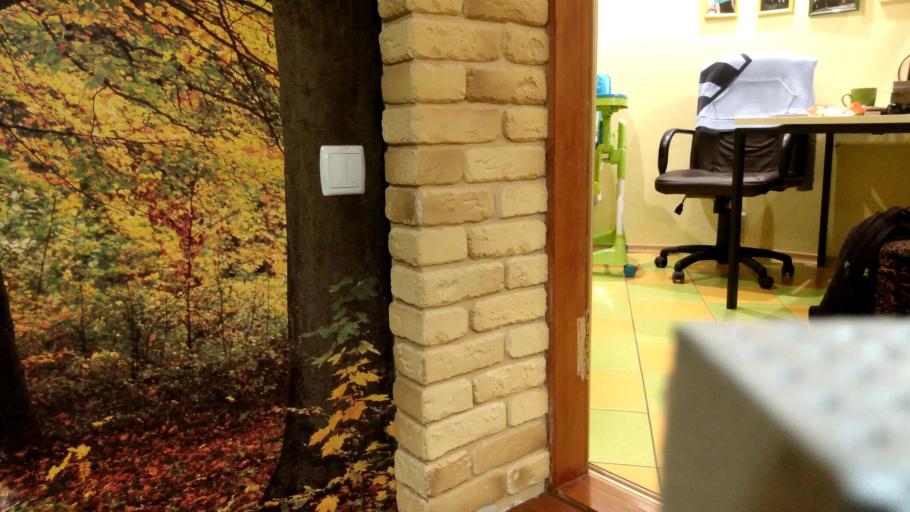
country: RU
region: Republic of Karelia
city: Pudozh
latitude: 61.7460
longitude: 37.6913
